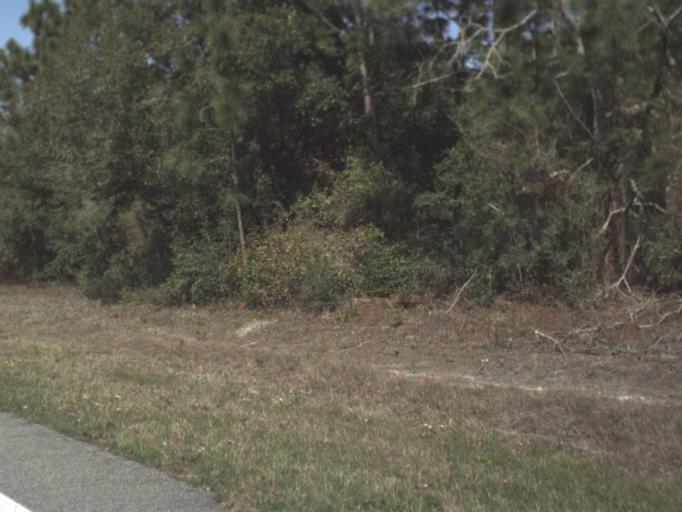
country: US
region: Florida
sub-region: Wakulla County
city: Crawfordville
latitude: 29.9565
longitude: -84.3851
